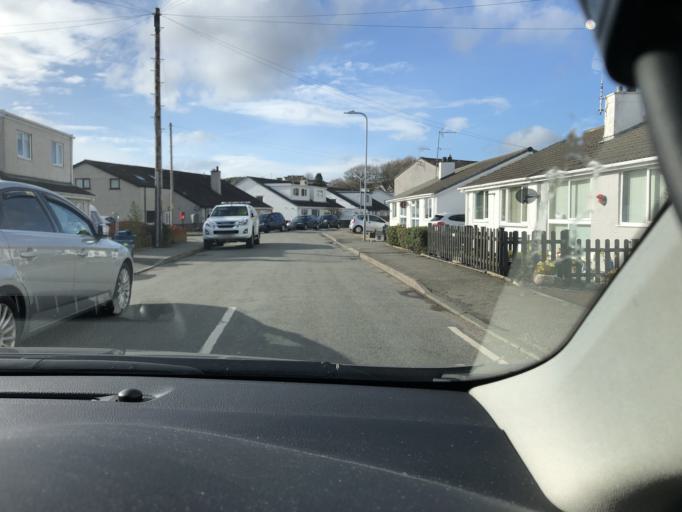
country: GB
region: Wales
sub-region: Anglesey
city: Menai Bridge
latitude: 53.2308
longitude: -4.1700
